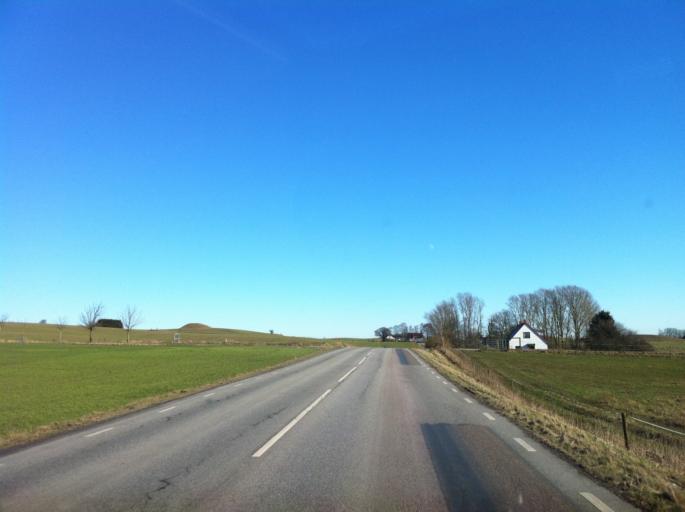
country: SE
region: Skane
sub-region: Svedala Kommun
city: Klagerup
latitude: 55.5782
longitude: 13.1939
